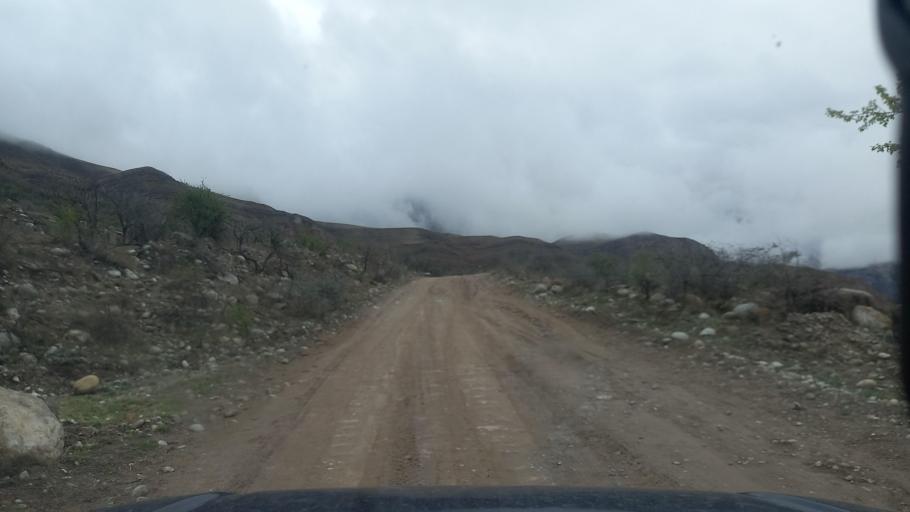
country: RU
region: Kabardino-Balkariya
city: Bylym
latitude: 43.4608
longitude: 43.0107
